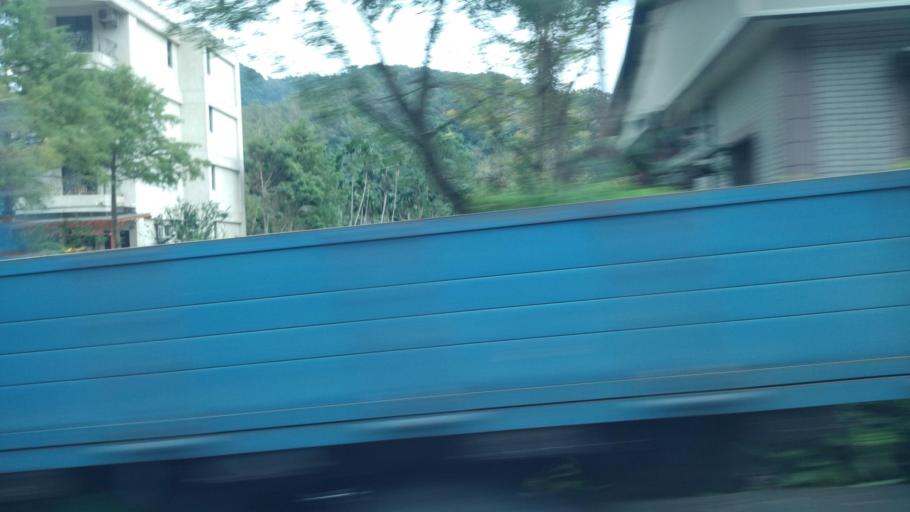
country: TW
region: Taiwan
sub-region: Hualien
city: Hualian
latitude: 23.9215
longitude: 121.5039
